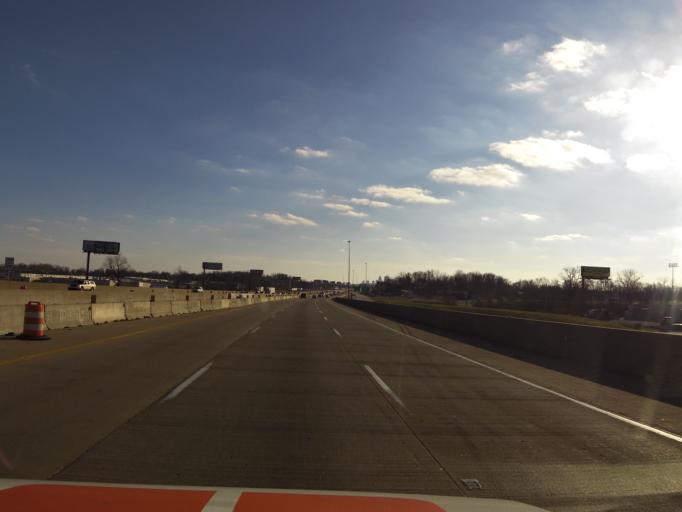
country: US
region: Indiana
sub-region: Clark County
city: Clarksville
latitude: 38.3159
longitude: -85.7527
